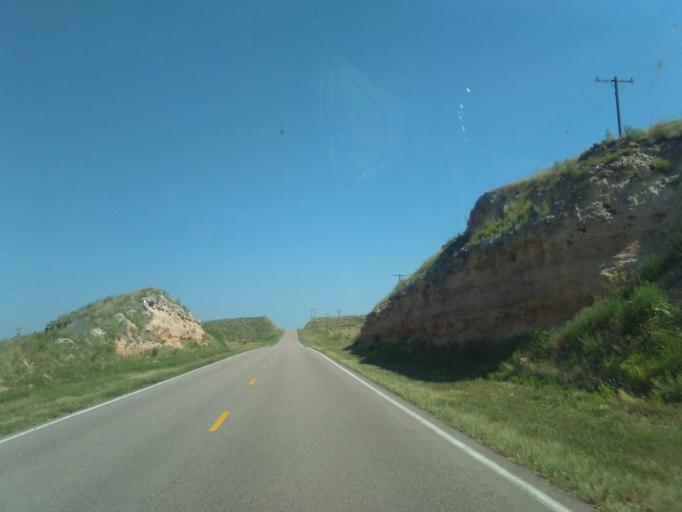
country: US
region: Nebraska
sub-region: Dundy County
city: Benkelman
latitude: 39.8610
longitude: -101.5412
